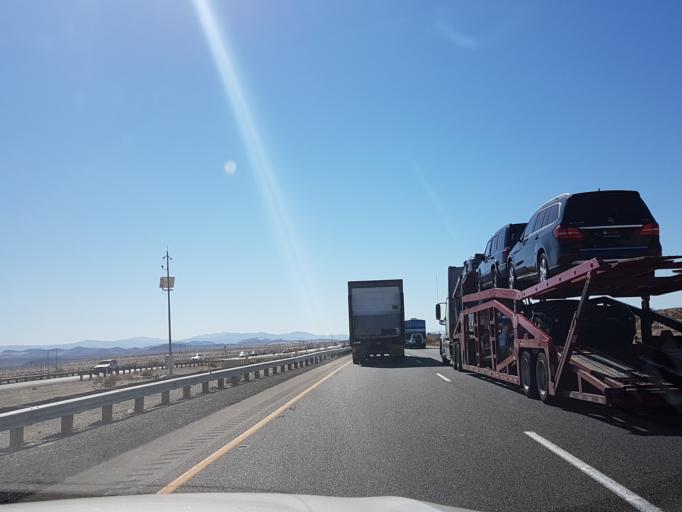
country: US
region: California
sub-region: San Bernardino County
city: Fort Irwin
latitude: 35.0445
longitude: -116.4531
